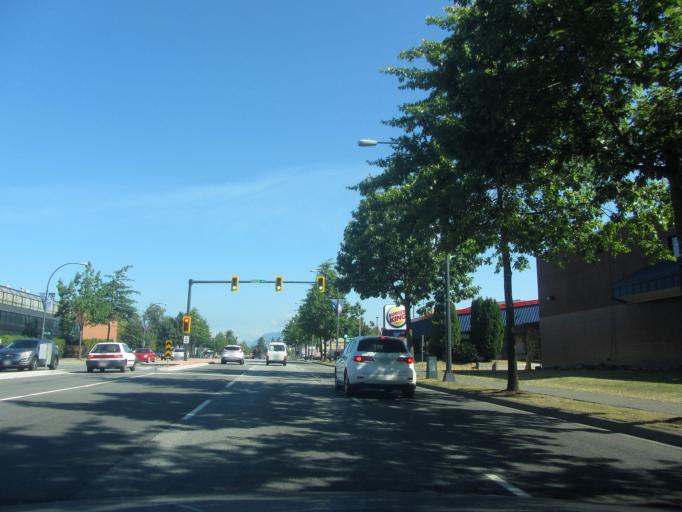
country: CA
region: British Columbia
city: New Westminster
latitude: 49.1898
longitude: -122.8454
